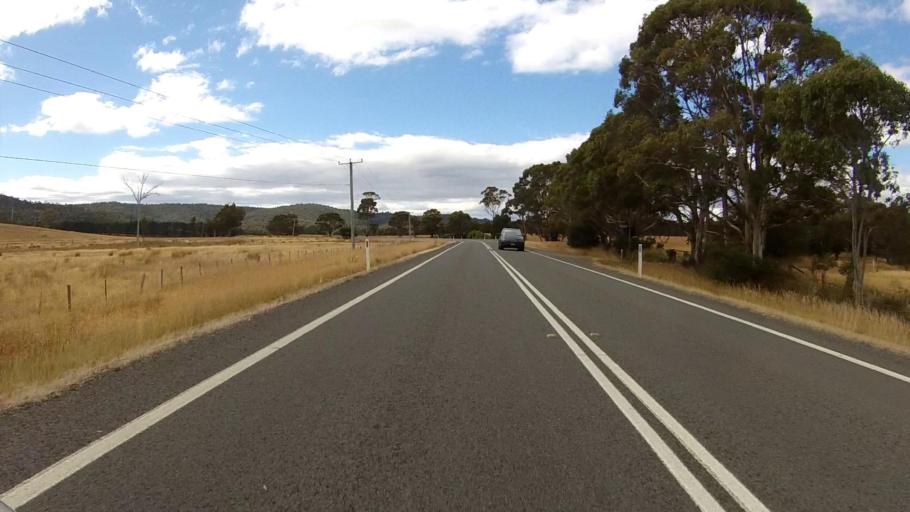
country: AU
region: Tasmania
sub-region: Sorell
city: Sorell
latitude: -42.6398
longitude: 147.5843
